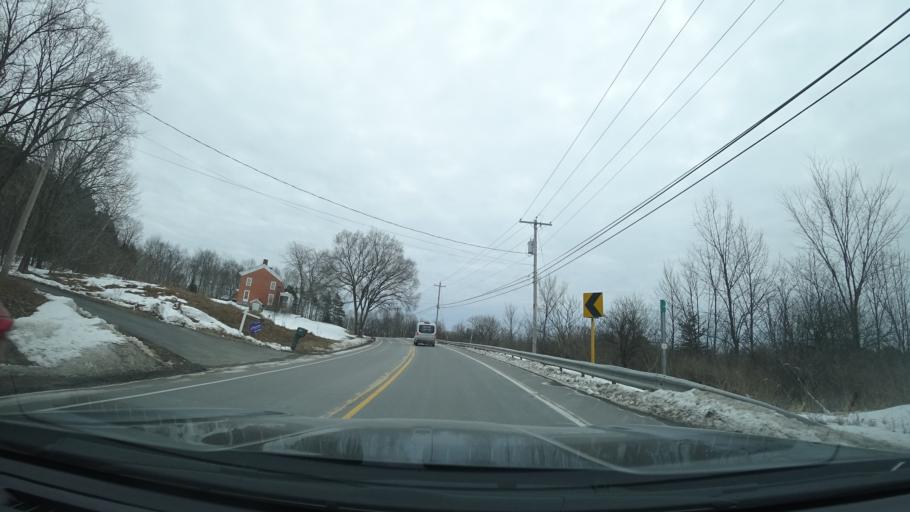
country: US
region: New York
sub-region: Washington County
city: Fort Edward
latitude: 43.2504
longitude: -73.5001
